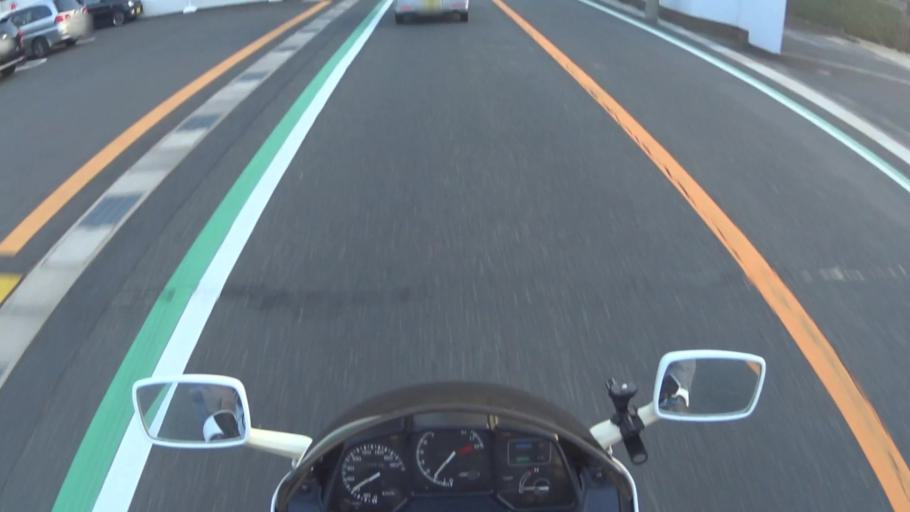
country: JP
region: Kyoto
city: Miyazu
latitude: 35.6763
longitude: 135.0282
